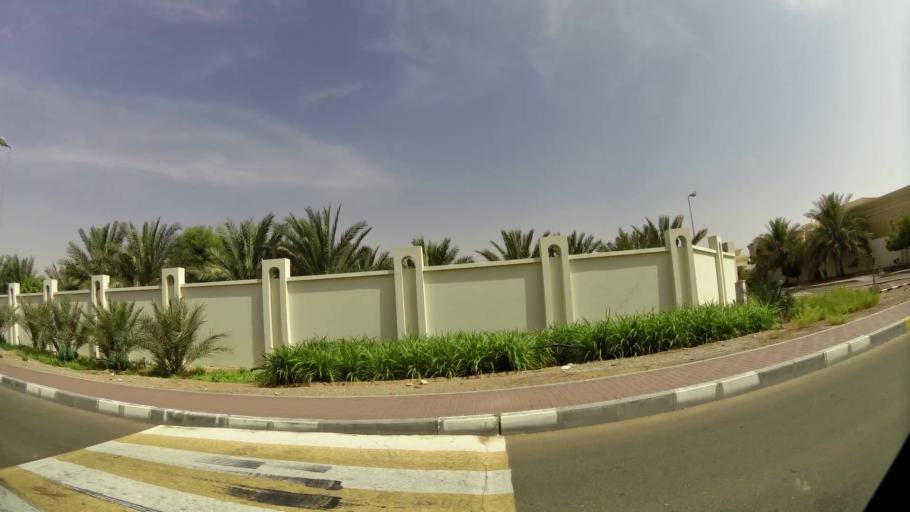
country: AE
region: Abu Dhabi
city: Al Ain
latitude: 24.1575
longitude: 55.6793
